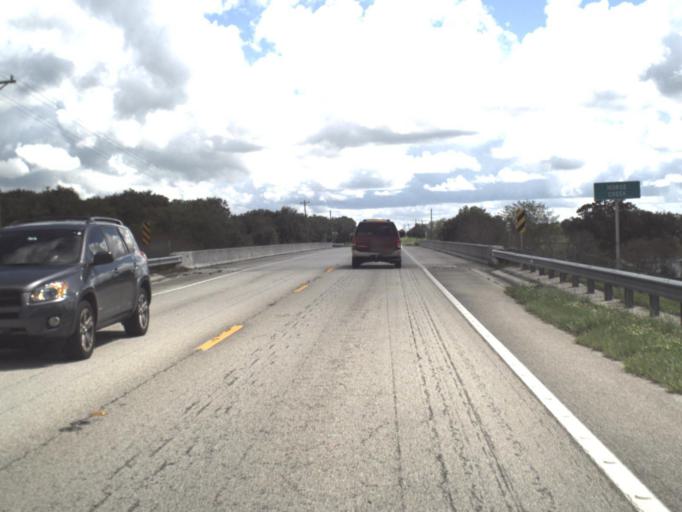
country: US
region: Florida
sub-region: DeSoto County
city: Arcadia
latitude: 27.2557
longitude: -81.9689
